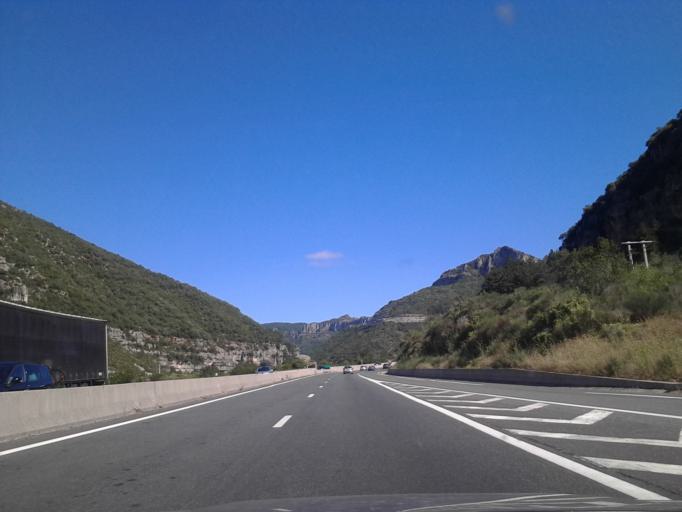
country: FR
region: Languedoc-Roussillon
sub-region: Departement de l'Herault
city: Lodeve
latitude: 43.7969
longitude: 3.3262
